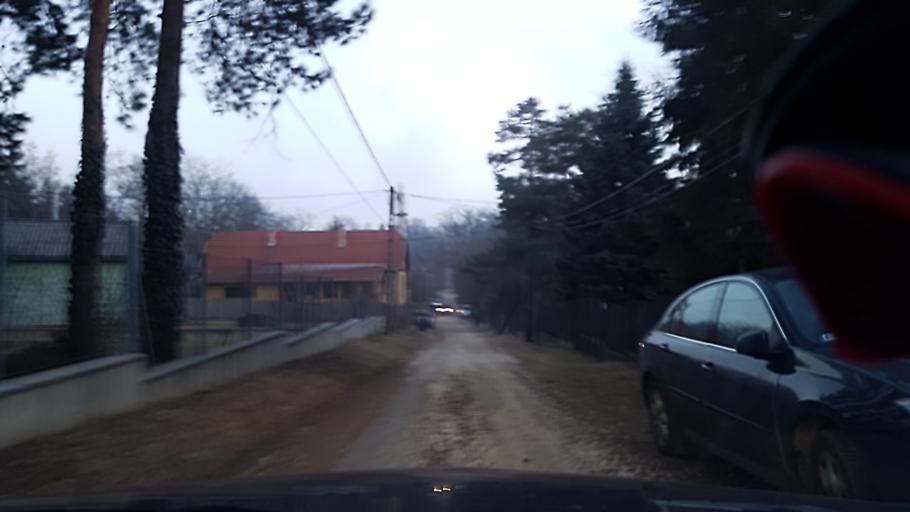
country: HU
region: Pest
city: Piliscsaba
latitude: 47.6431
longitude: 18.8263
